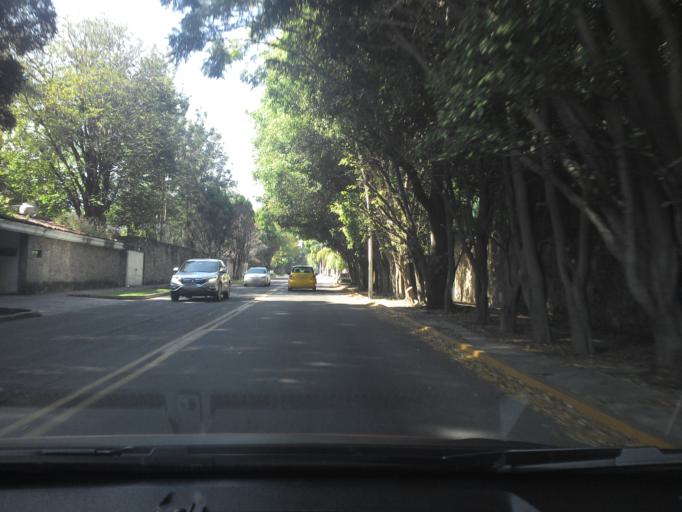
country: MX
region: Jalisco
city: Zapopan2
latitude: 20.6950
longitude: -103.3995
